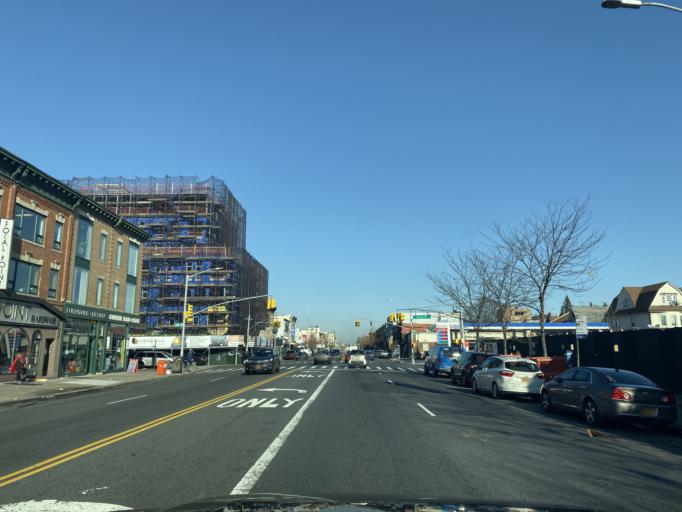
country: US
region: New York
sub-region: Kings County
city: Bensonhurst
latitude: 40.6094
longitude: -73.9622
